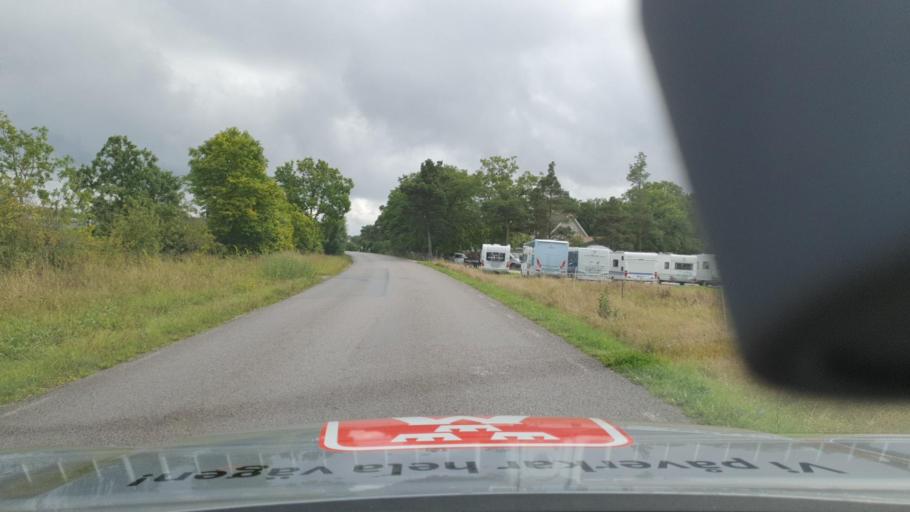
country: SE
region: Gotland
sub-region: Gotland
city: Slite
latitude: 57.6847
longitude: 18.7645
